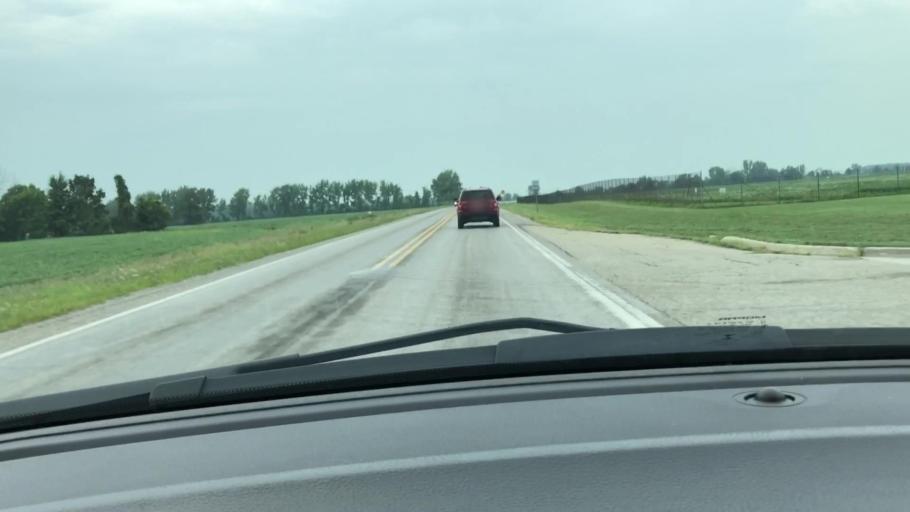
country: US
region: Michigan
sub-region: Saginaw County
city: Freeland
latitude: 43.5340
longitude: -84.0952
